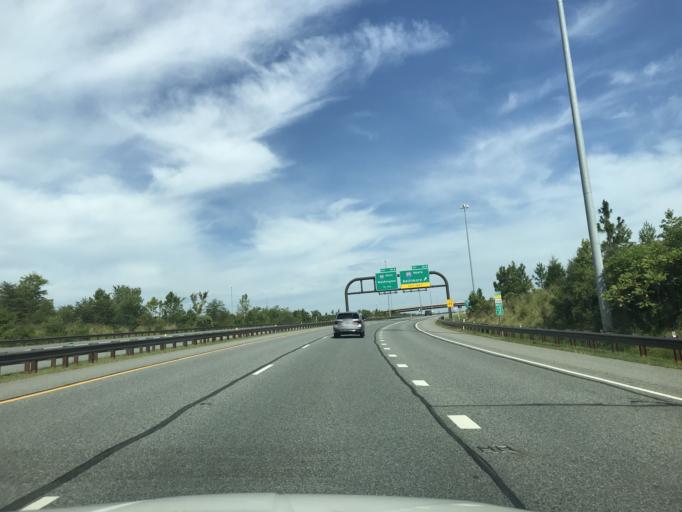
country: US
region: Maryland
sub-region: Prince George's County
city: West Laurel
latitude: 39.0686
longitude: -76.9006
